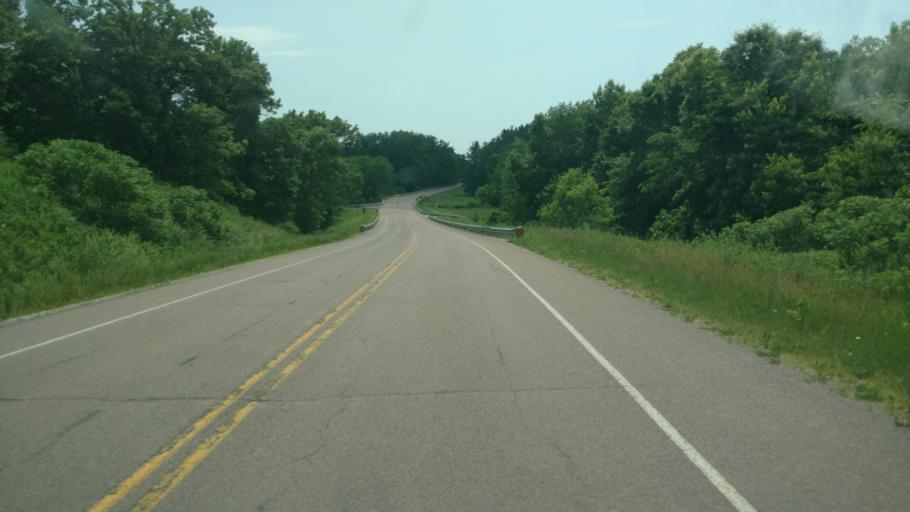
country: US
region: Wisconsin
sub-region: Monroe County
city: Cashton
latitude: 43.6539
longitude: -90.5940
